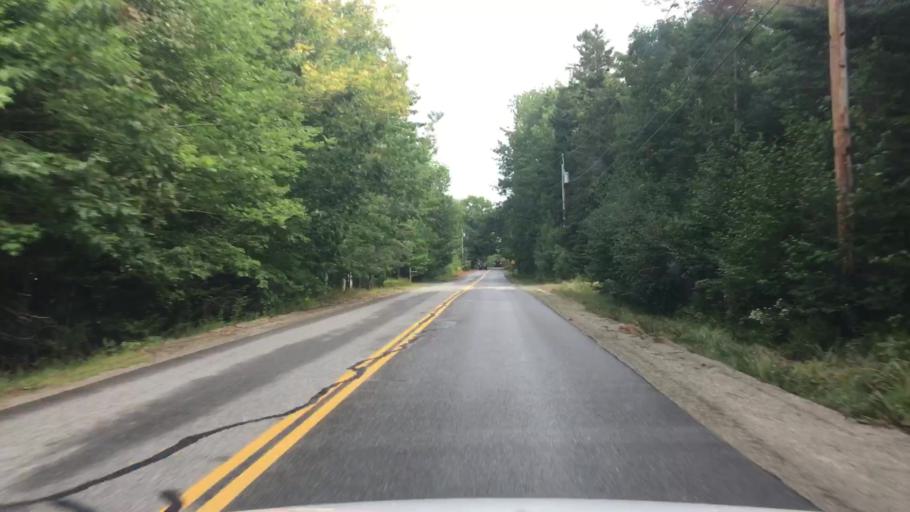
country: US
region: Maine
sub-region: Hancock County
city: Trenton
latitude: 44.4375
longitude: -68.4005
